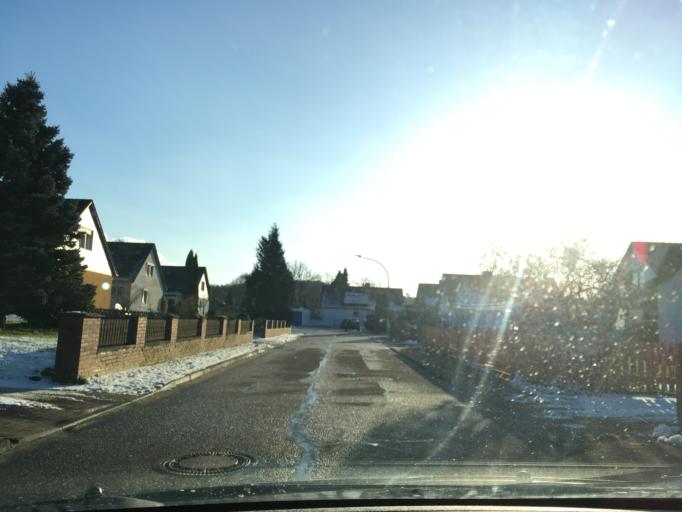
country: DE
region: Schleswig-Holstein
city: Buchen
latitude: 53.4868
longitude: 10.5966
